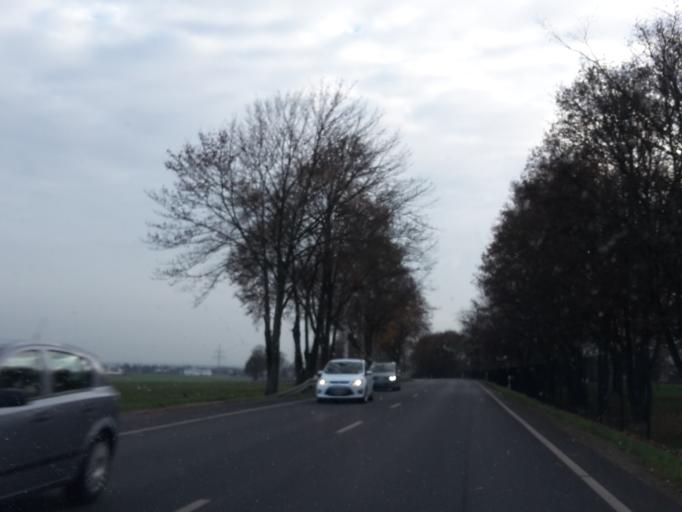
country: DE
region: Hesse
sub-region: Regierungsbezirk Darmstadt
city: Wiesbaden
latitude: 50.0741
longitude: 8.2727
